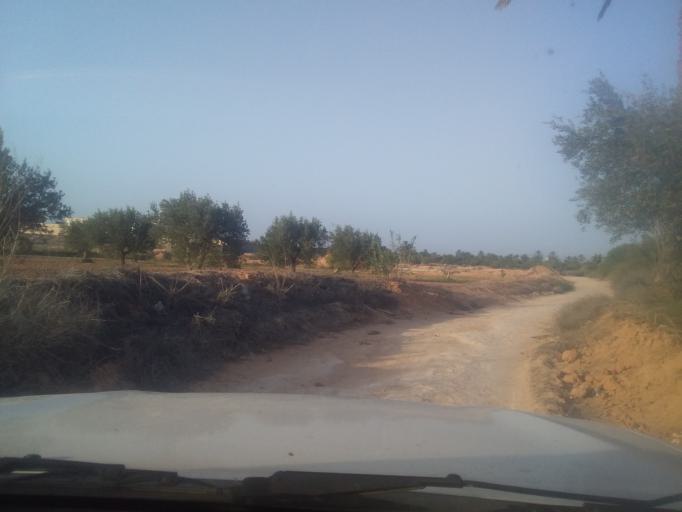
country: TN
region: Qabis
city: Gabes
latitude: 33.6319
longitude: 10.2920
